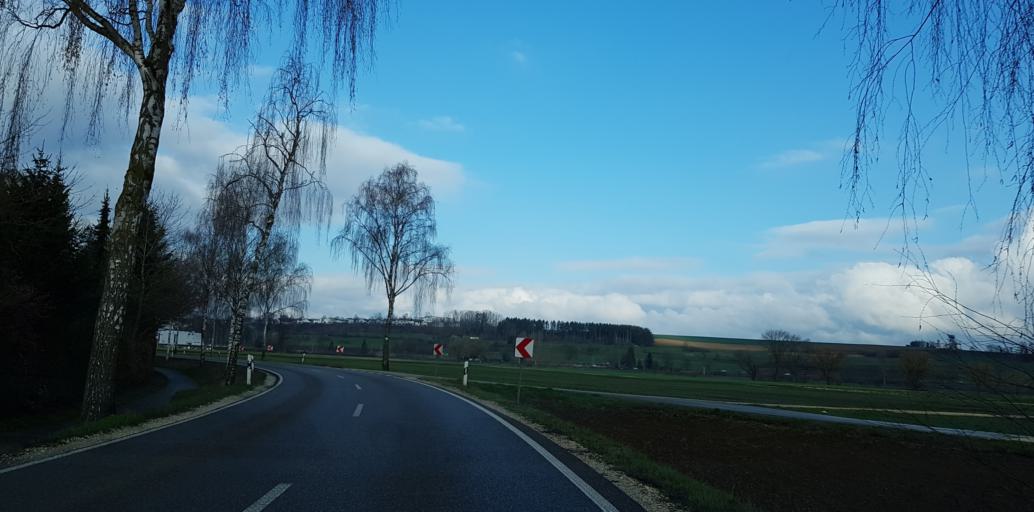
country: DE
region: Baden-Wuerttemberg
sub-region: Tuebingen Region
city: Erbach
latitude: 48.3321
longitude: 9.9167
